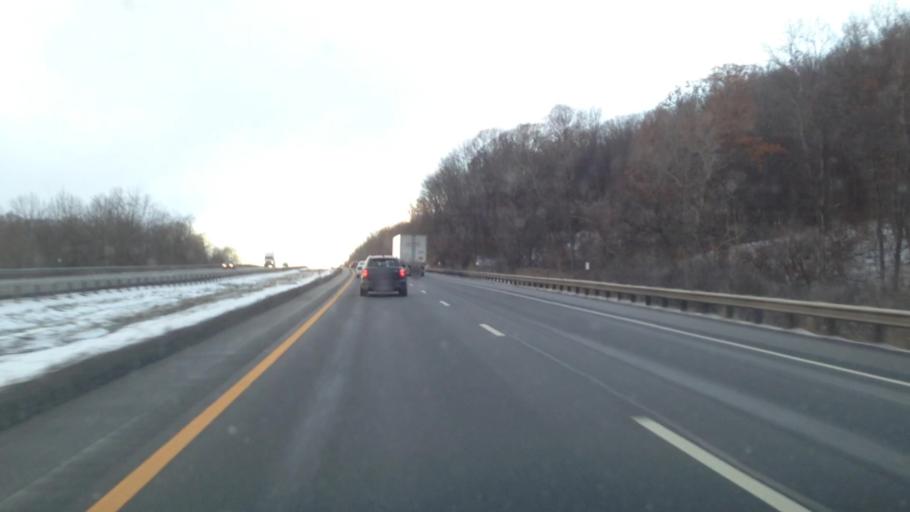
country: US
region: New York
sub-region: Herkimer County
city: Ilion
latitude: 43.0245
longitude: -75.0257
